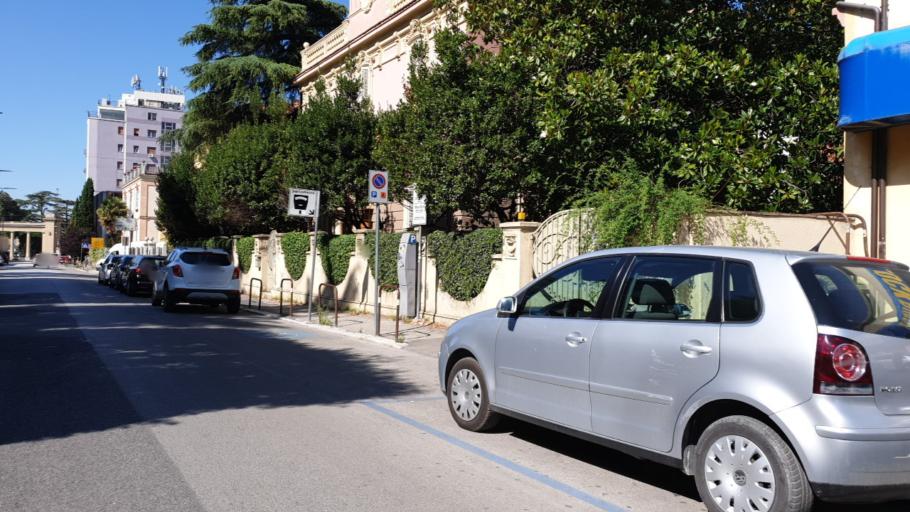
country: IT
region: Umbria
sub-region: Provincia di Perugia
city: Foligno
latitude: 42.9546
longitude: 12.7082
